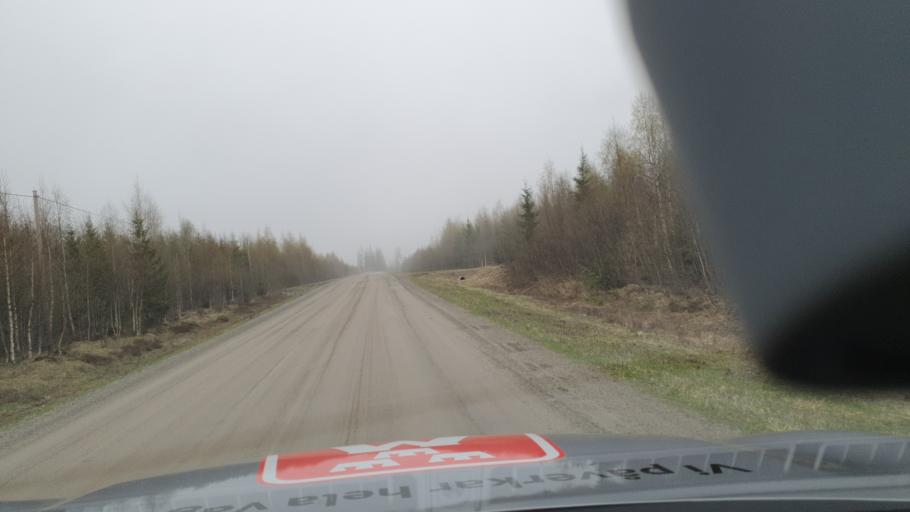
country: SE
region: Vaesternorrland
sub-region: OErnskoeldsviks Kommun
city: Husum
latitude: 63.6050
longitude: 19.0245
